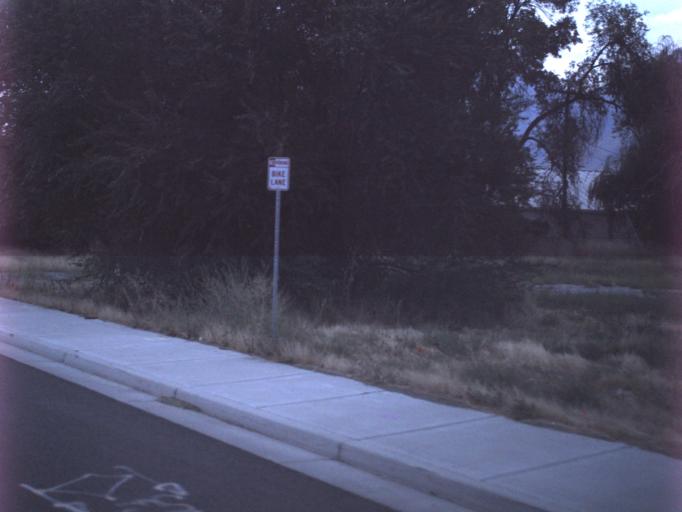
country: US
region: Utah
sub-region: Utah County
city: Lindon
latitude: 40.3428
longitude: -111.7208
